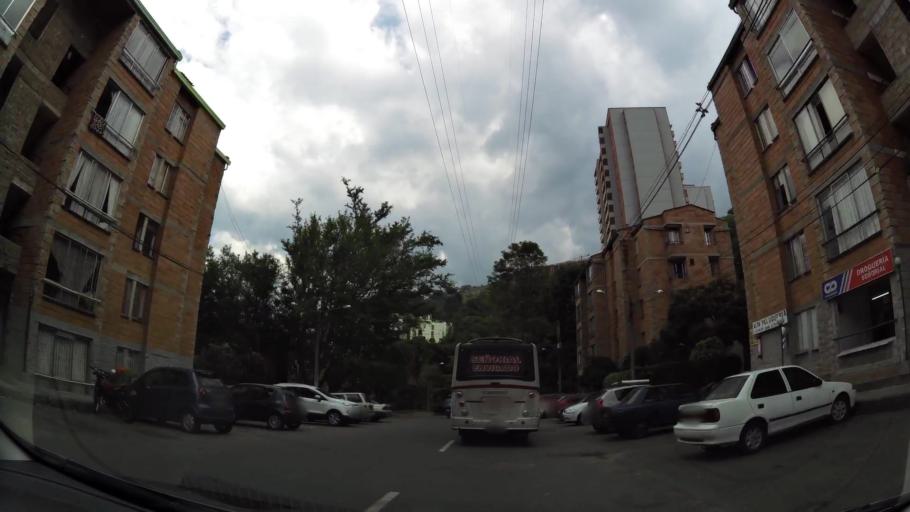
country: CO
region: Antioquia
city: Envigado
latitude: 6.1590
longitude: -75.5980
